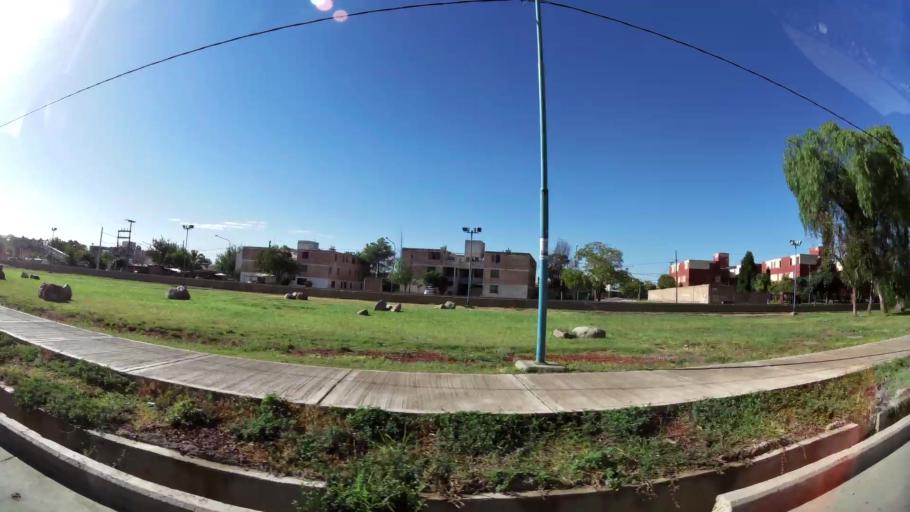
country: AR
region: Mendoza
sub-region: Departamento de Godoy Cruz
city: Godoy Cruz
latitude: -32.9245
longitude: -68.8659
